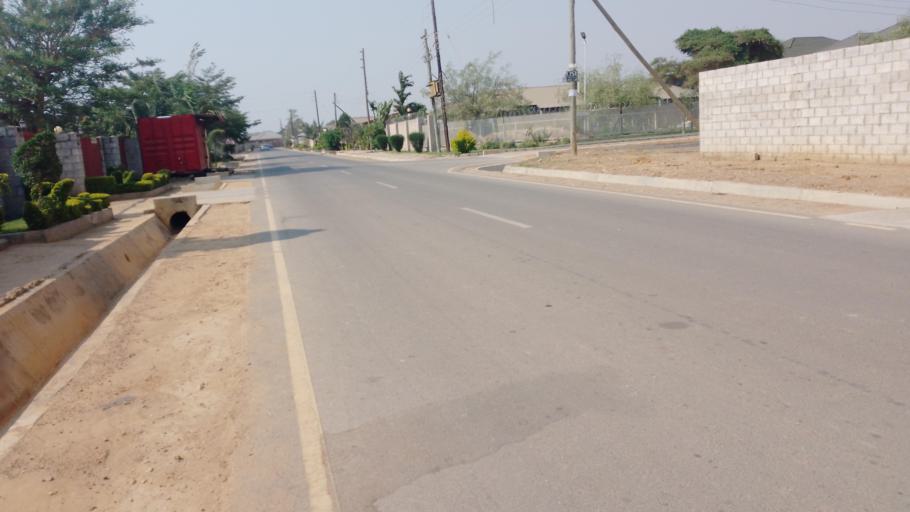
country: ZM
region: Lusaka
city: Lusaka
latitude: -15.3892
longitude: 28.3914
